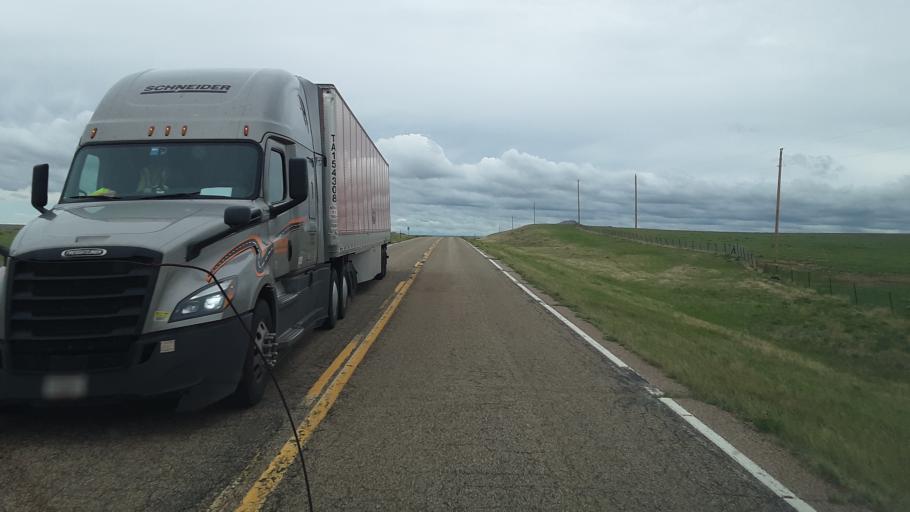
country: US
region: Colorado
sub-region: Lincoln County
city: Limon
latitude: 38.8378
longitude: -103.8218
